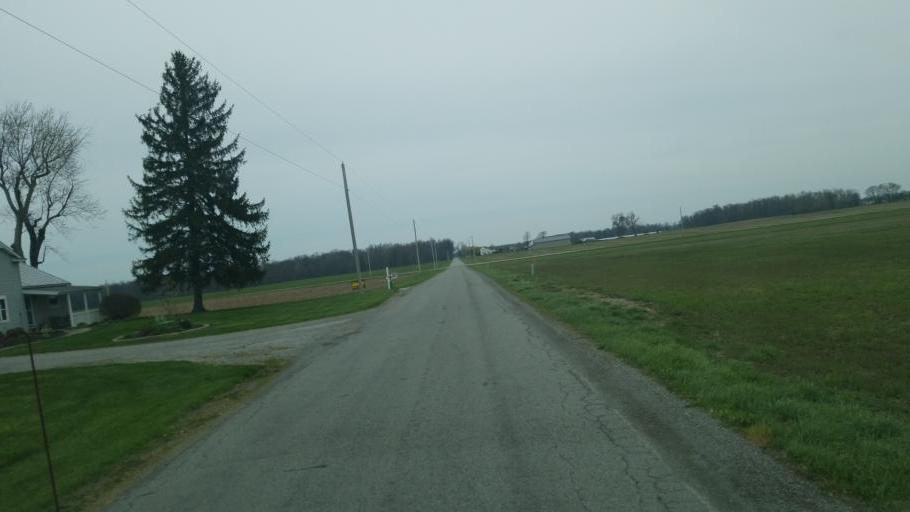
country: US
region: Ohio
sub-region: Wyandot County
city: Carey
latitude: 40.9611
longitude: -83.5130
